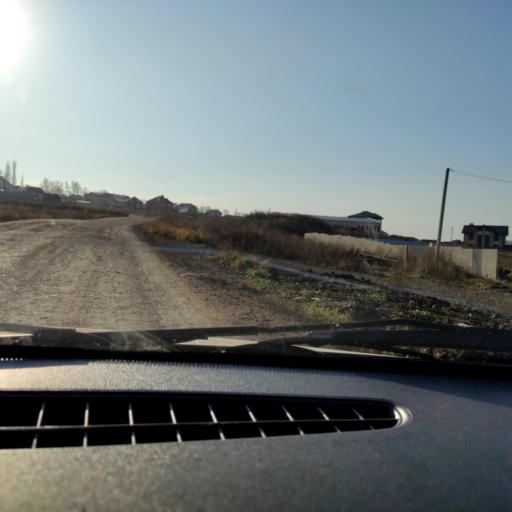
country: RU
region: Bashkortostan
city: Kabakovo
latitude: 54.6352
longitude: 56.0741
